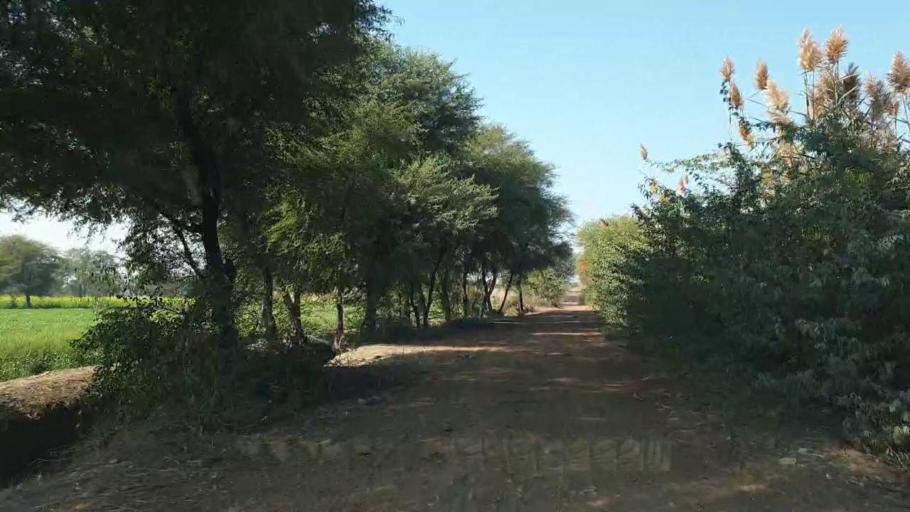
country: PK
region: Sindh
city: Nawabshah
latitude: 26.0660
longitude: 68.4766
